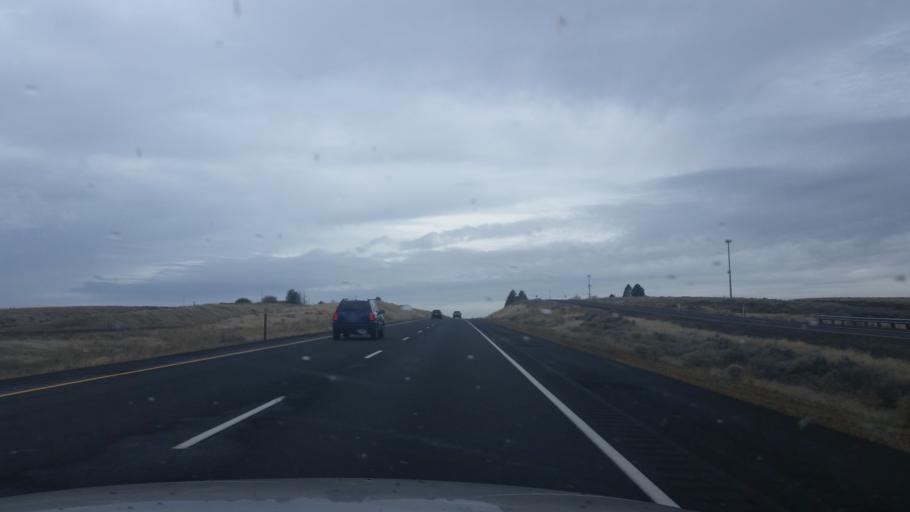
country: US
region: Washington
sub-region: Grant County
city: Warden
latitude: 47.0862
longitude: -118.8380
